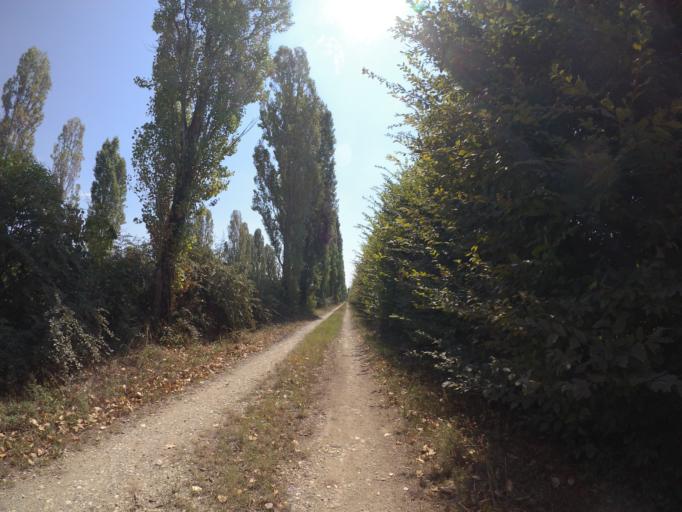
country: IT
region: Friuli Venezia Giulia
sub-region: Provincia di Udine
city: Codroipo
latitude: 45.9584
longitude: 13.0108
